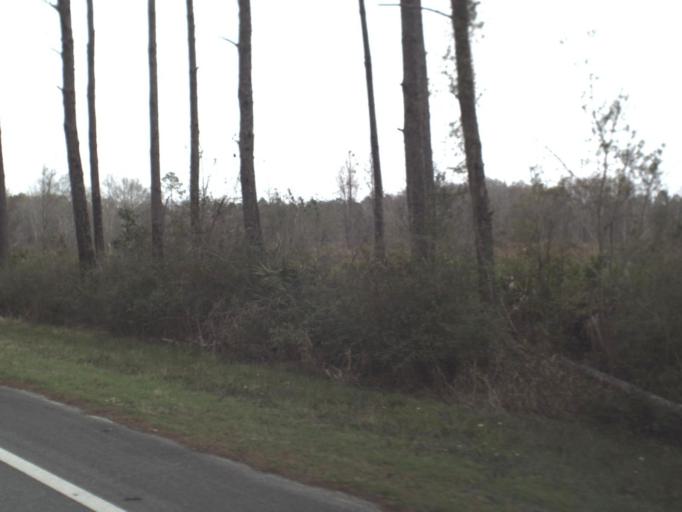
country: US
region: Florida
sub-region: Leon County
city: Woodville
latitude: 30.1965
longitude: -84.1929
